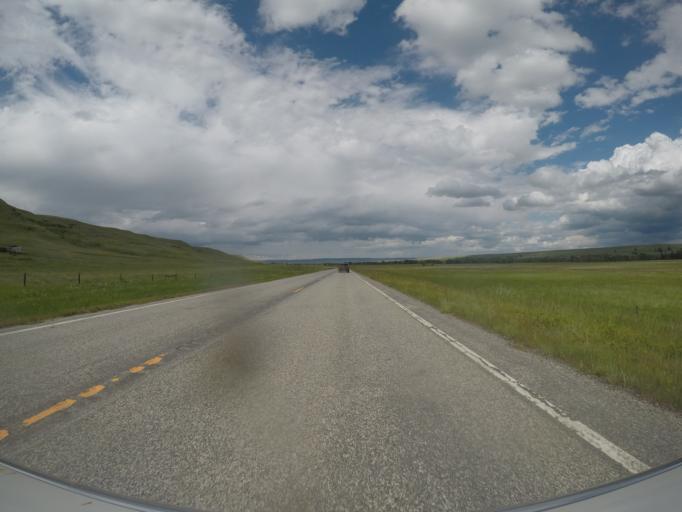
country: US
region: Montana
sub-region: Sweet Grass County
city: Big Timber
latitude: 45.7889
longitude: -109.9779
